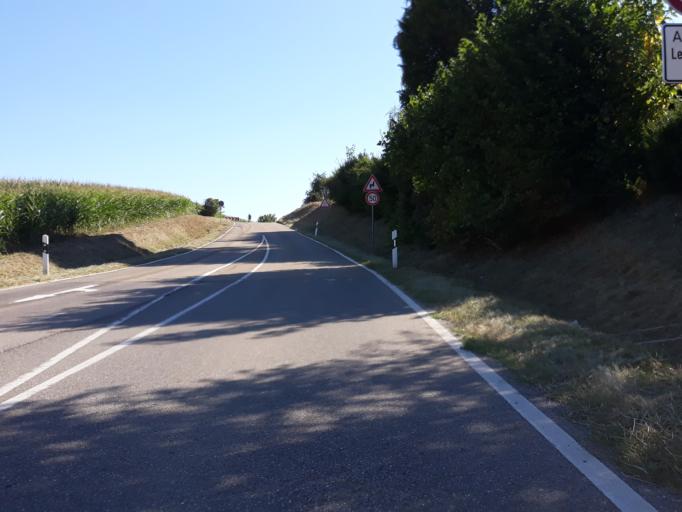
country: DE
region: Baden-Wuerttemberg
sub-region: Regierungsbezirk Stuttgart
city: Aidlingen
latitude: 48.7126
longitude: 8.8958
